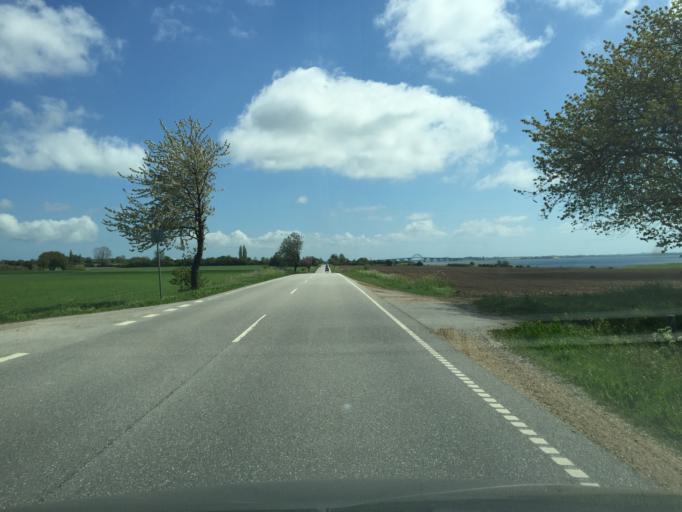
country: DK
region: Zealand
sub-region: Guldborgsund Kommune
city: Stubbekobing
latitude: 54.9976
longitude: 12.1115
